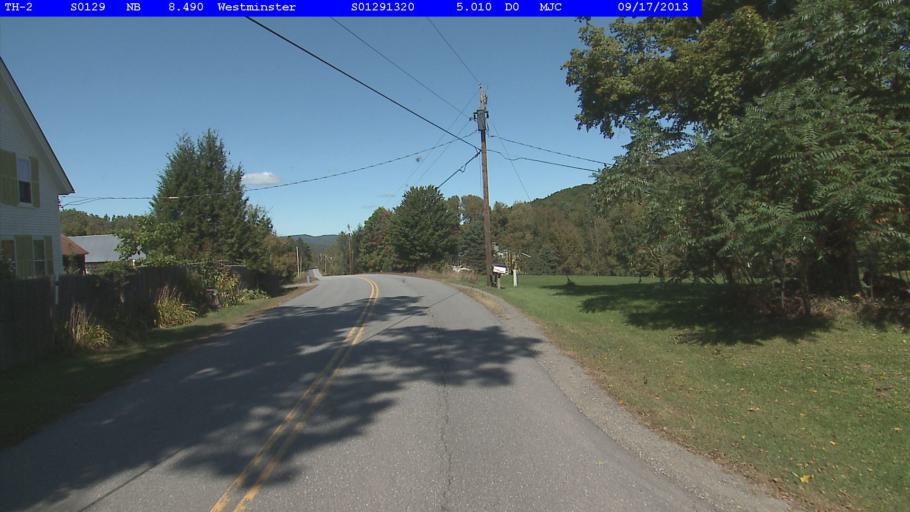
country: US
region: Vermont
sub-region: Windham County
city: Bellows Falls
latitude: 43.0871
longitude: -72.5353
